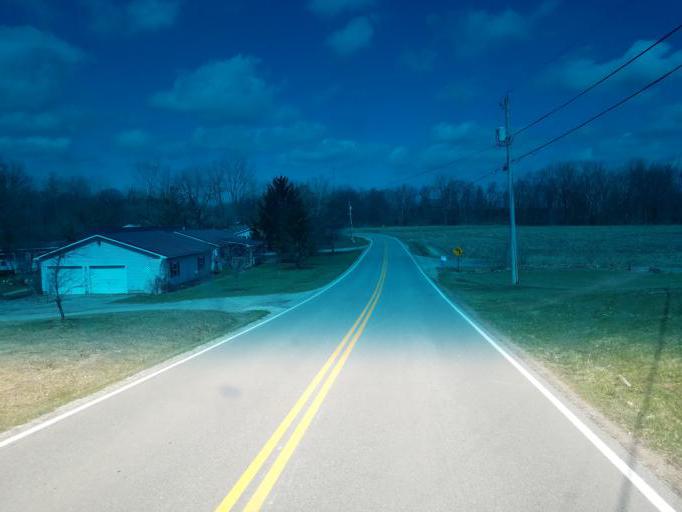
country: US
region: Ohio
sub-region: Crawford County
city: Bucyrus
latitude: 40.8019
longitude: -83.0032
